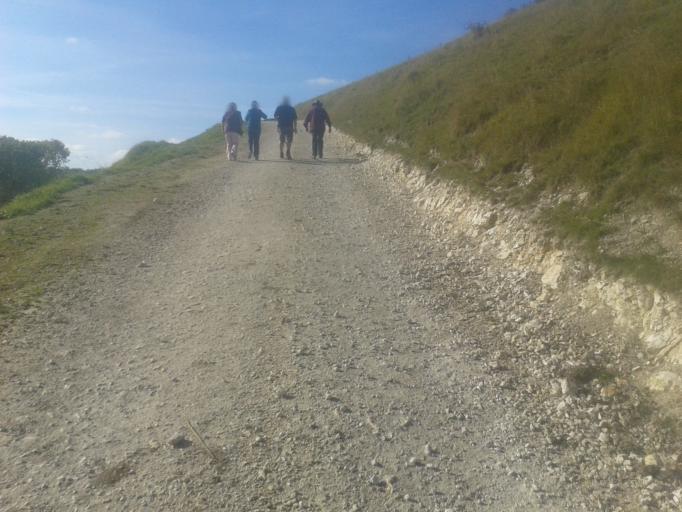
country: GB
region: England
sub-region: North Yorkshire
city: Thixendale
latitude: 54.0401
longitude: -0.7189
